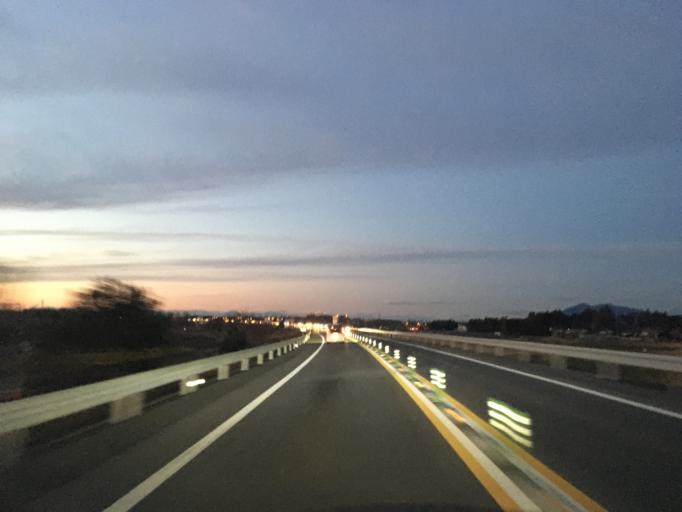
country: JP
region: Ibaraki
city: Naka
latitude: 36.0492
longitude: 140.1055
